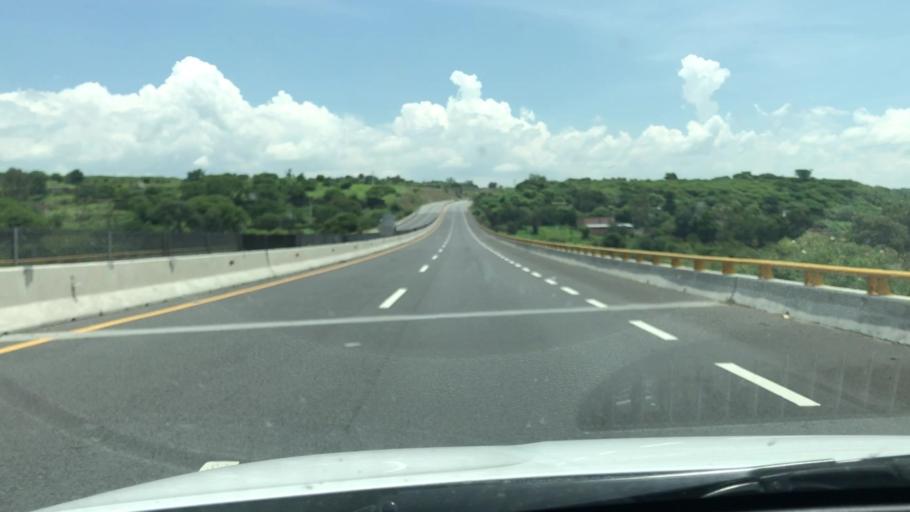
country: MX
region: Jalisco
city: Degollado
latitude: 20.3775
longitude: -102.1225
